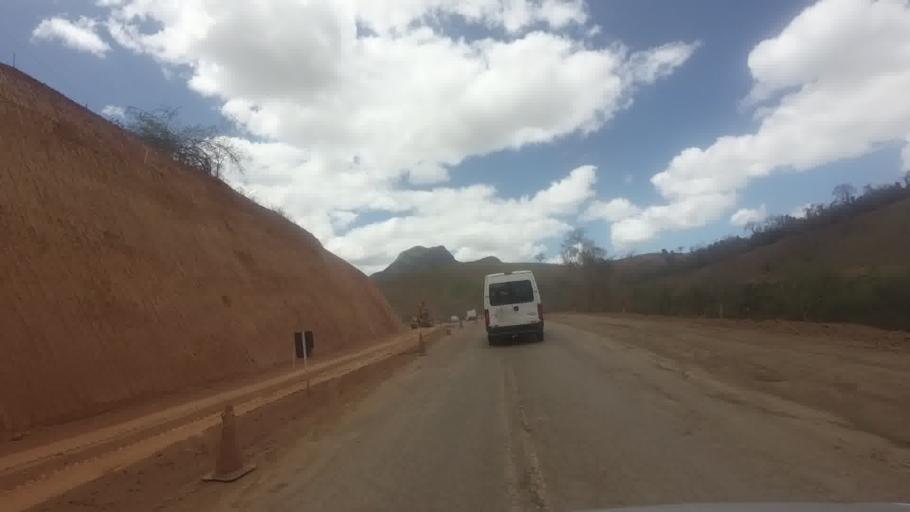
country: BR
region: Rio de Janeiro
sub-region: Santo Antonio De Padua
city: Santo Antonio de Padua
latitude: -21.5144
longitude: -42.0945
